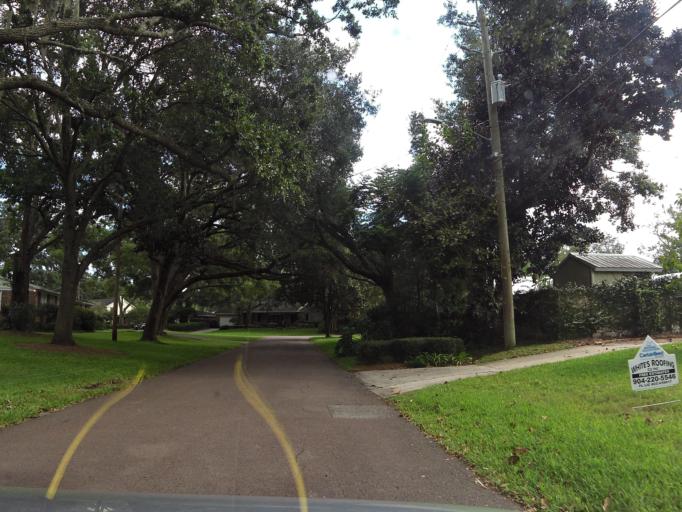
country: US
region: Florida
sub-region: Clay County
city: Bellair-Meadowbrook Terrace
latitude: 30.2571
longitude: -81.7086
